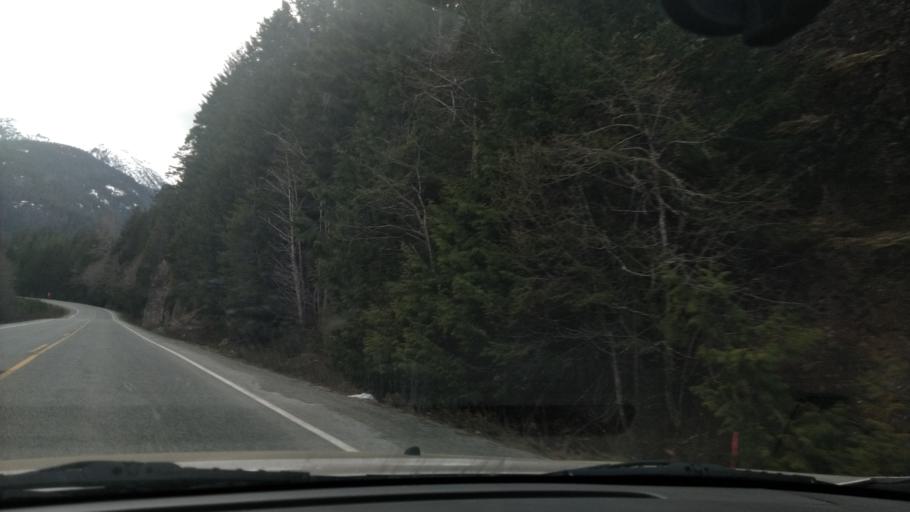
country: CA
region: British Columbia
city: Campbell River
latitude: 49.8452
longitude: -125.8579
